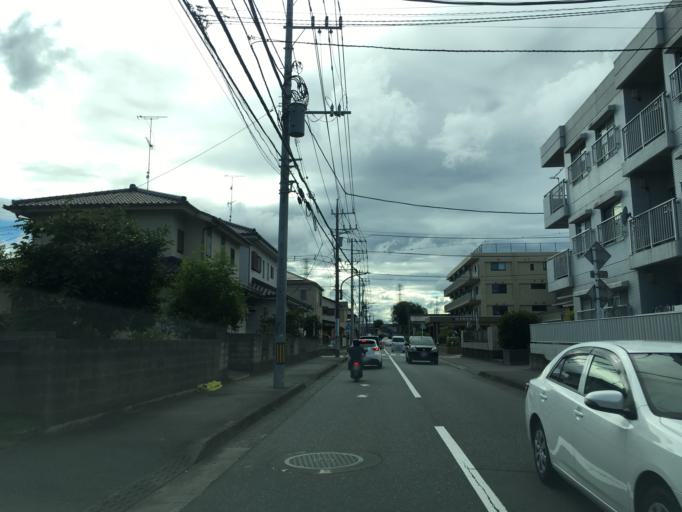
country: JP
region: Tokyo
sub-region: Machida-shi
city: Machida
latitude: 35.5608
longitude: 139.4079
